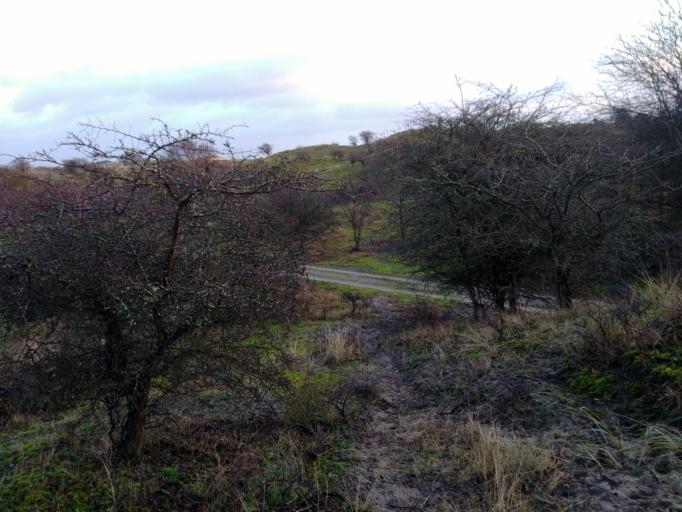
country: NL
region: South Holland
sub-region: Gemeente Noordwijkerhout
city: Noordwijkerhout
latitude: 52.3089
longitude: 4.5046
